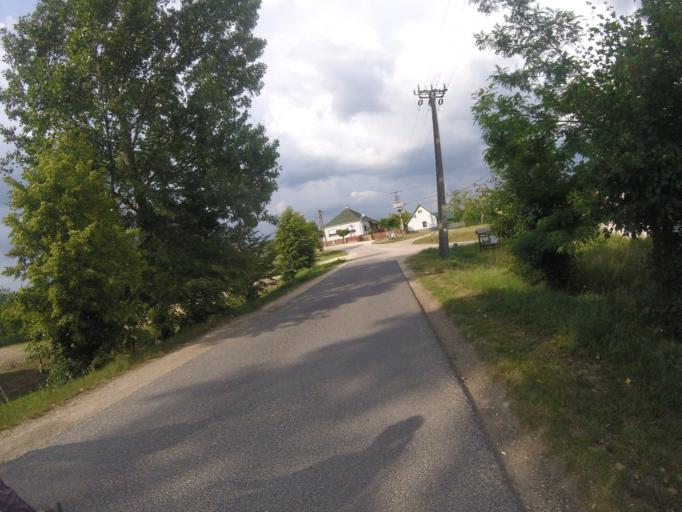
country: HU
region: Fejer
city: Szarliget
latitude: 47.4795
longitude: 18.5209
